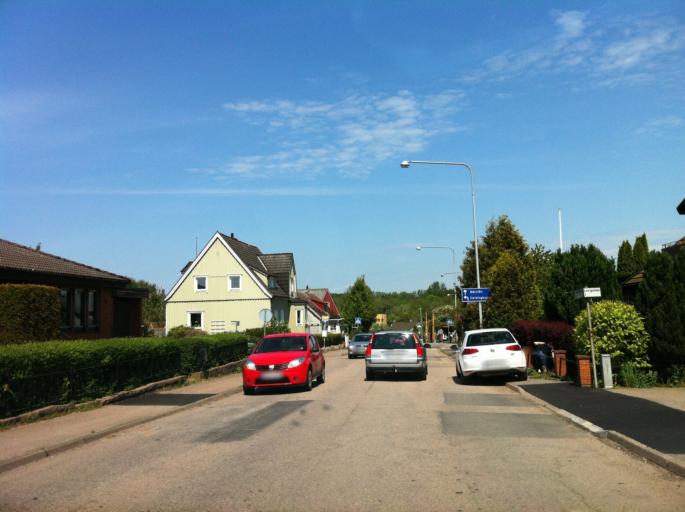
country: SE
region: Skane
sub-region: Helsingborg
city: Glumslov
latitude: 55.9225
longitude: 12.8501
